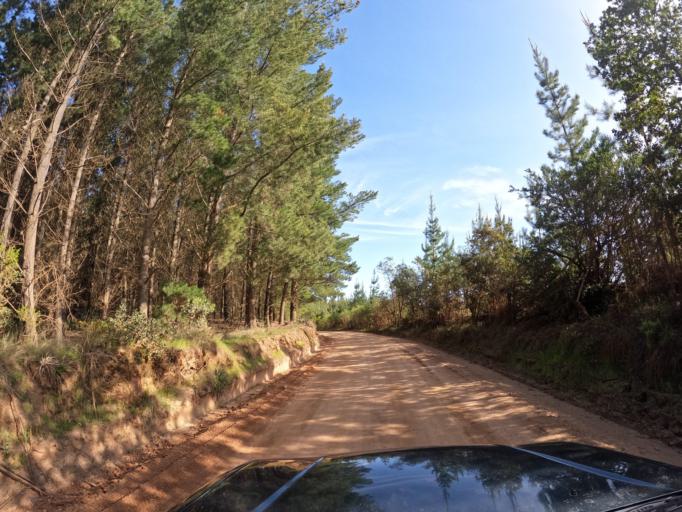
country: CL
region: Biobio
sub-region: Provincia de Biobio
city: Yumbel
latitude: -37.1029
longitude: -72.7412
